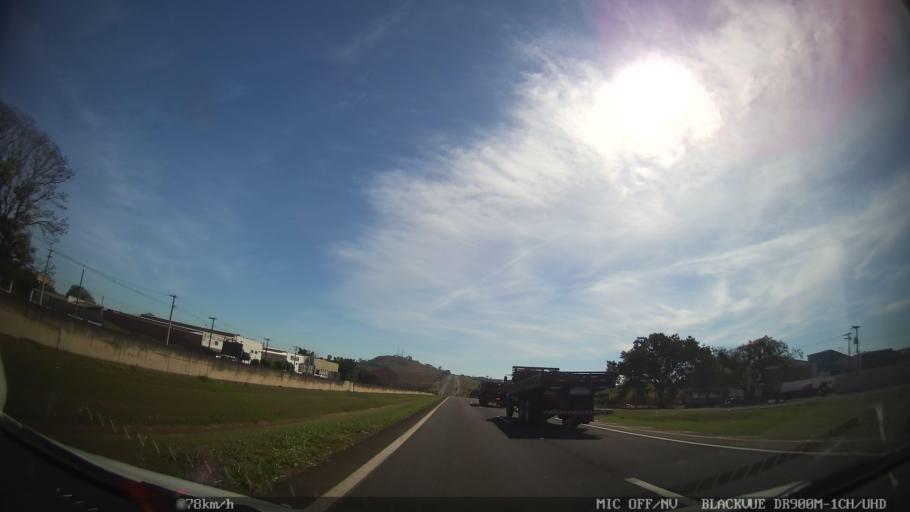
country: BR
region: Sao Paulo
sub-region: Leme
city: Leme
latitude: -22.1747
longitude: -47.3989
